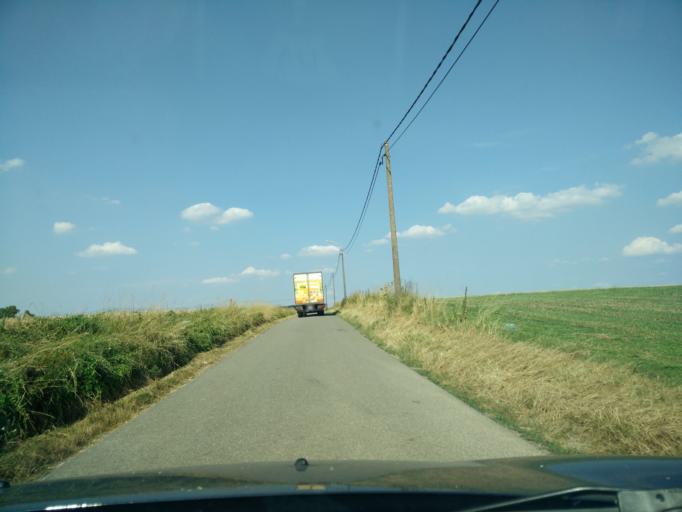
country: BE
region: Wallonia
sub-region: Province du Hainaut
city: Ecaussinnes-d'Enghien
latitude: 50.5758
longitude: 4.1951
